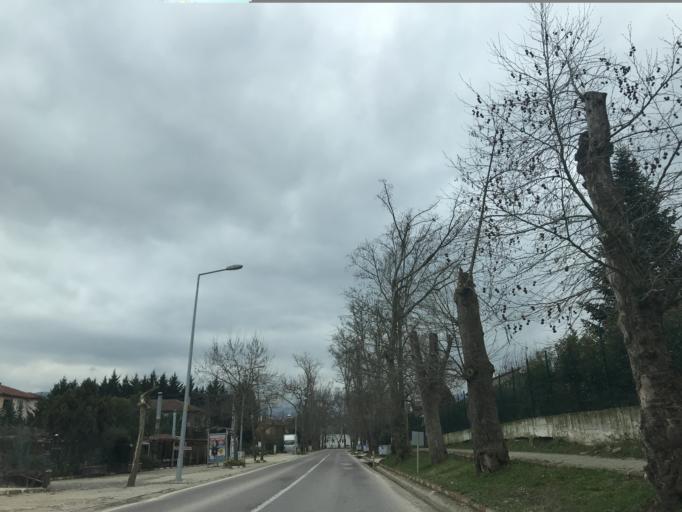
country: TR
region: Yalova
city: Kadikoy
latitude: 40.6316
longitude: 29.2237
